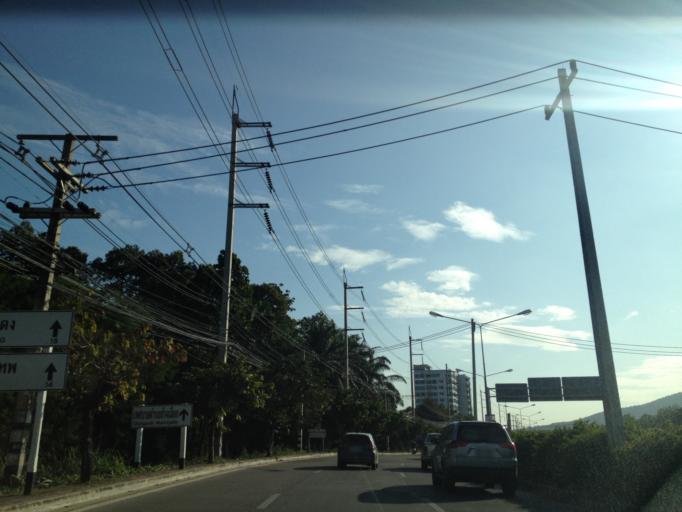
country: TH
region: Chiang Mai
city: Chiang Mai
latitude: 18.8220
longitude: 98.9653
